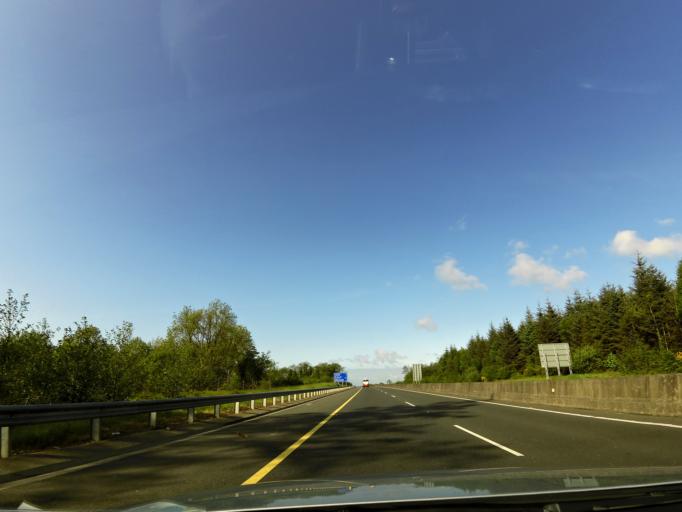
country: IE
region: Munster
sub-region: North Tipperary
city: Newport
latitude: 52.7519
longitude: -8.4214
